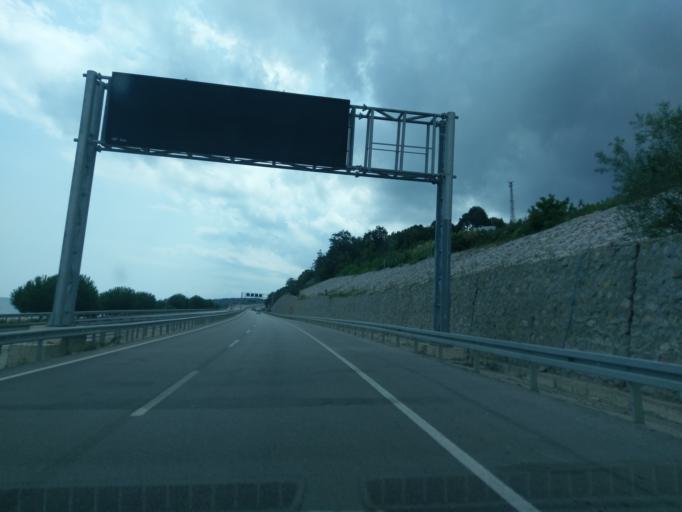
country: TR
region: Sinop
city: Gerze
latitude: 41.8301
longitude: 35.1602
